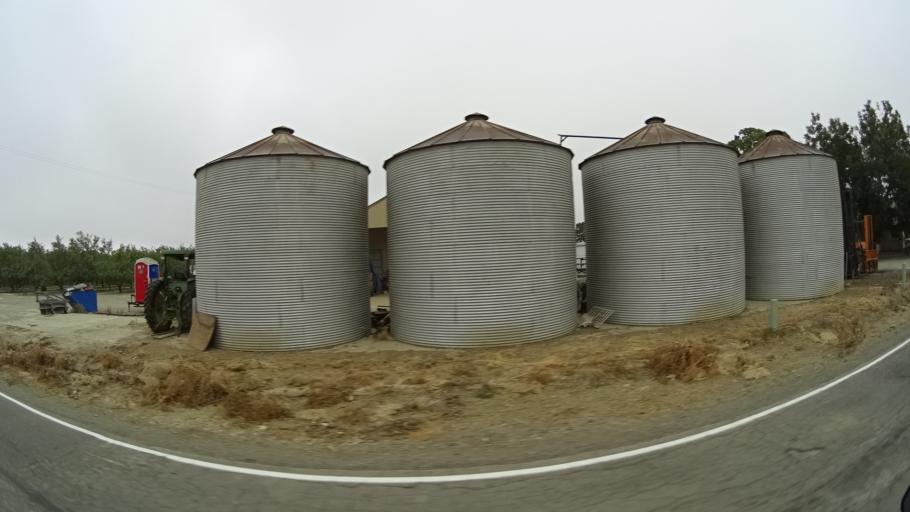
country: US
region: California
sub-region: Yolo County
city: Dunnigan
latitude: 38.9259
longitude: -122.0371
